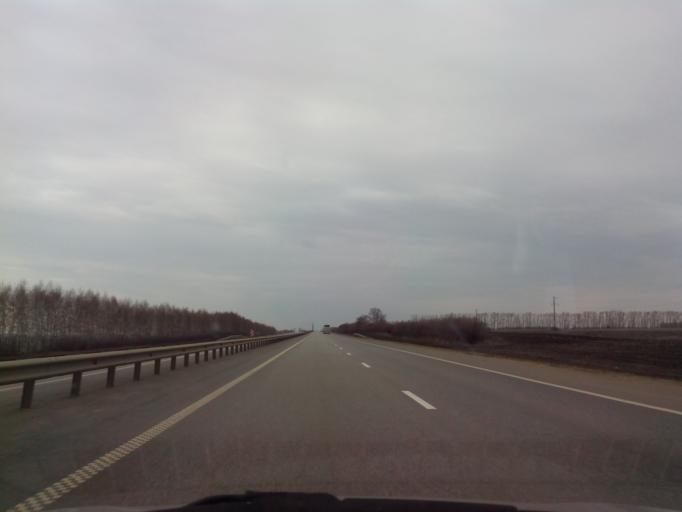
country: RU
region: Tambov
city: Zavoronezhskoye
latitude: 52.8421
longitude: 40.8376
